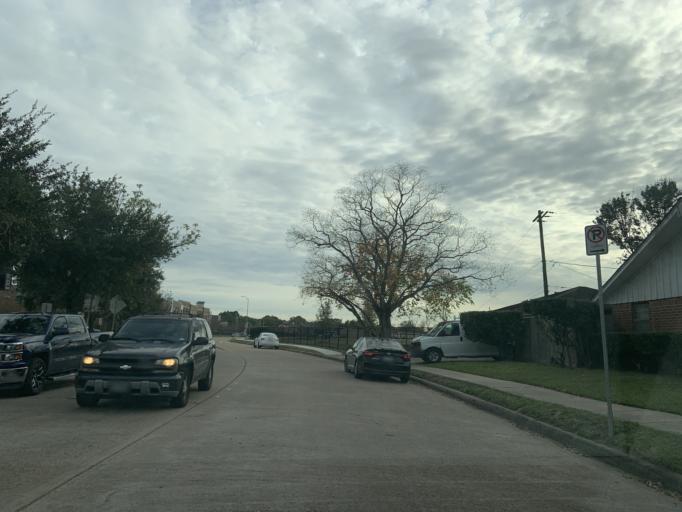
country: US
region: Texas
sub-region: Harris County
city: Bellaire
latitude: 29.6875
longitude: -95.5138
